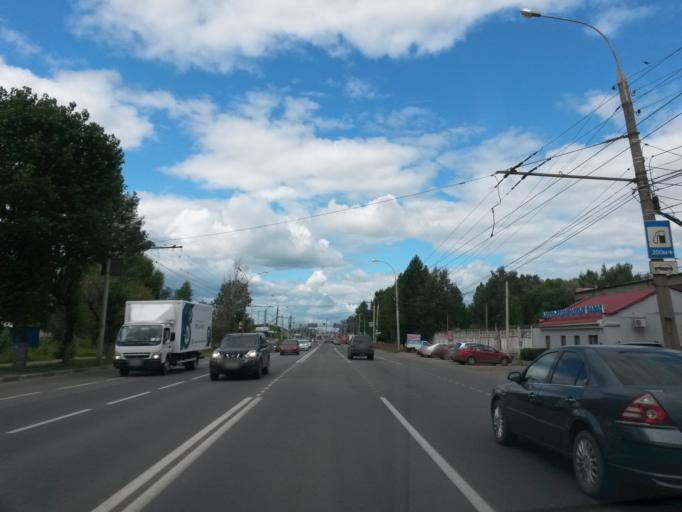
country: RU
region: Jaroslavl
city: Yaroslavl
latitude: 57.6606
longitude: 39.8438
